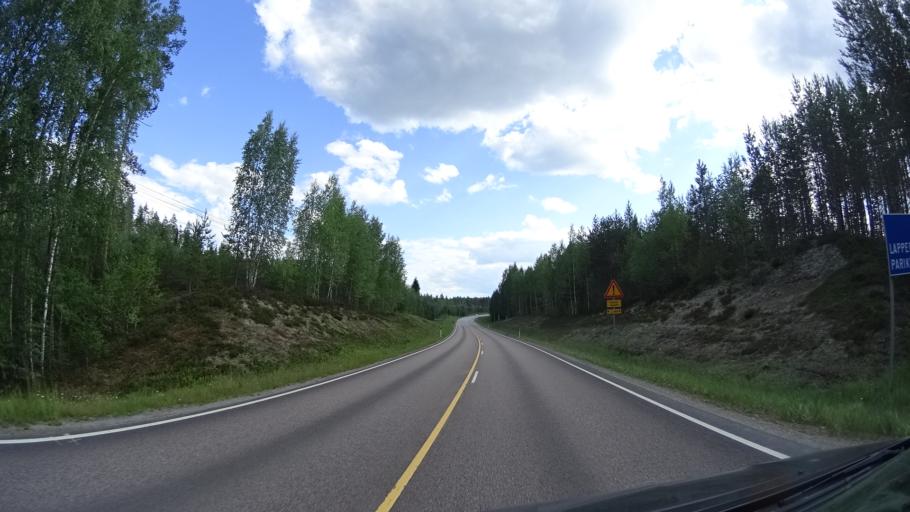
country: FI
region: Southern Savonia
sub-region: Savonlinna
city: Punkaharju
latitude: 61.6777
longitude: 29.4131
